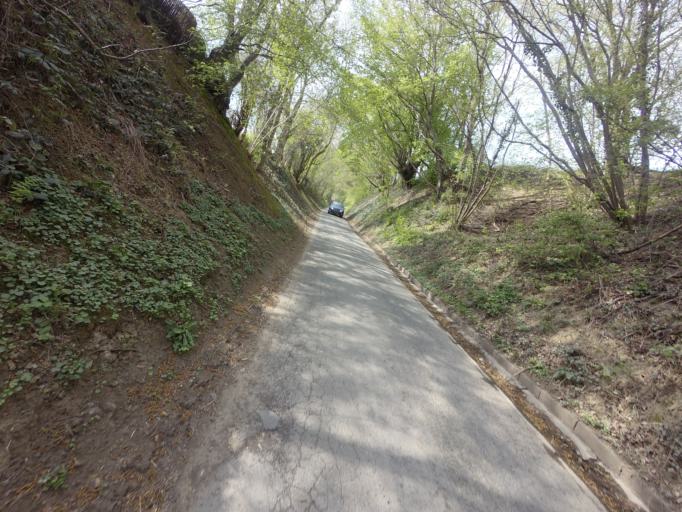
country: BE
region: Wallonia
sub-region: Province de Liege
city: La Calamine
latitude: 50.7194
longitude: 5.9962
